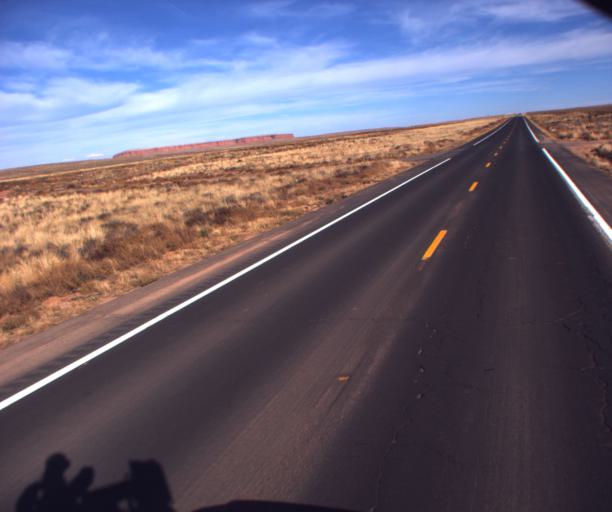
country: US
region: Arizona
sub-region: Apache County
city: Lukachukai
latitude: 36.9626
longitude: -109.4360
